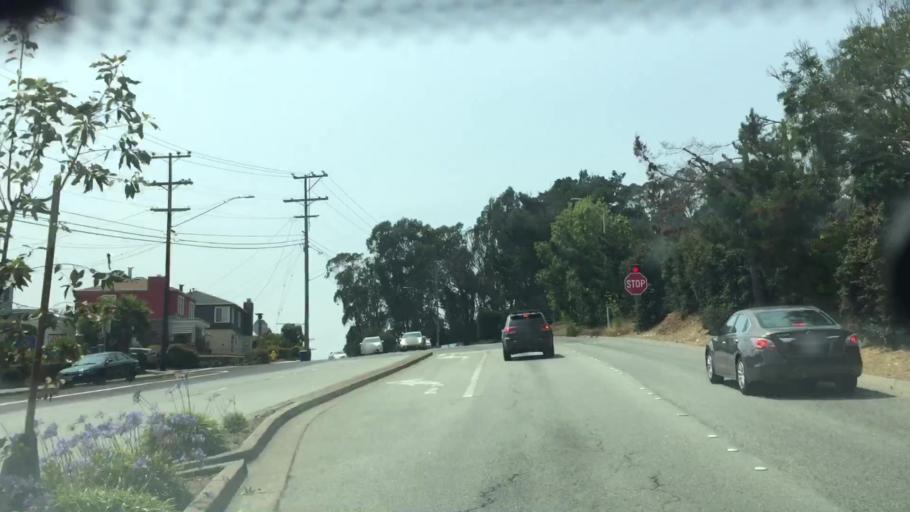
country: US
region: California
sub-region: San Mateo County
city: South San Francisco
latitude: 37.6686
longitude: -122.4236
